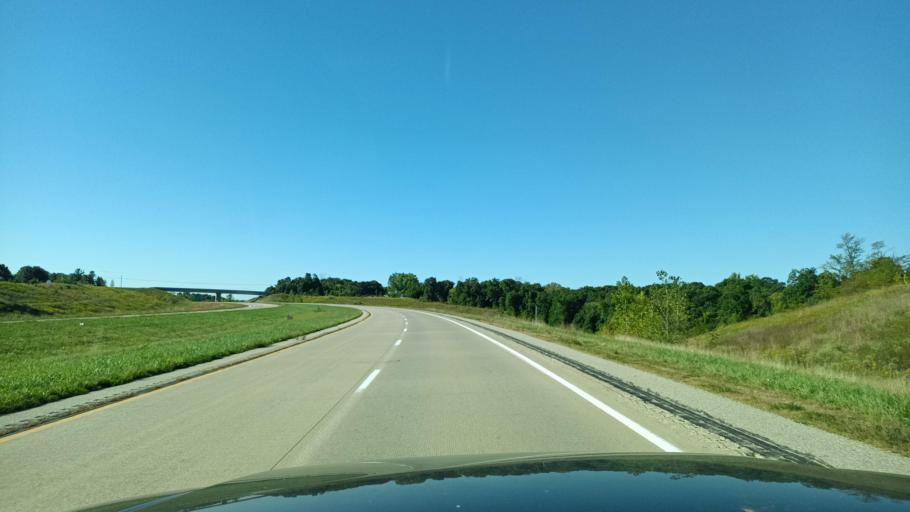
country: US
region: Iowa
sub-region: Lee County
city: Fort Madison
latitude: 40.6429
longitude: -91.3767
